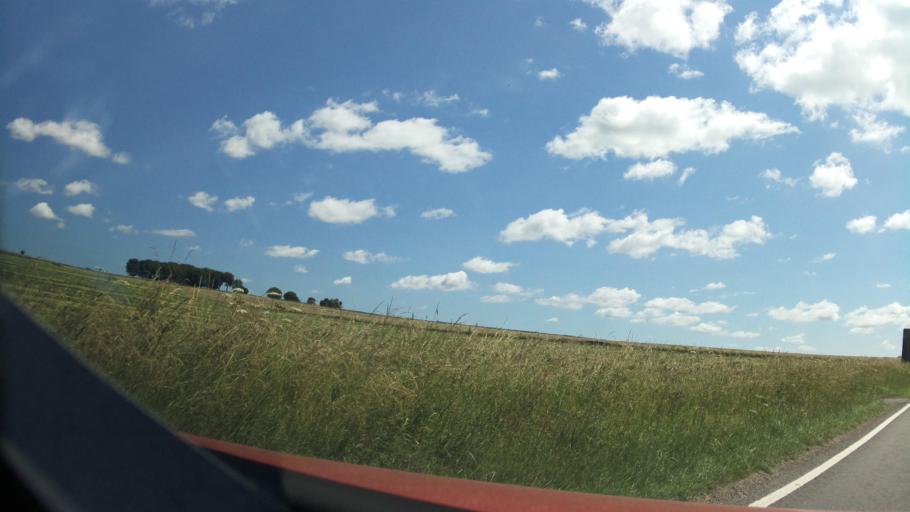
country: GB
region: England
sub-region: Derbyshire
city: Tideswell
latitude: 53.1690
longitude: -1.7796
